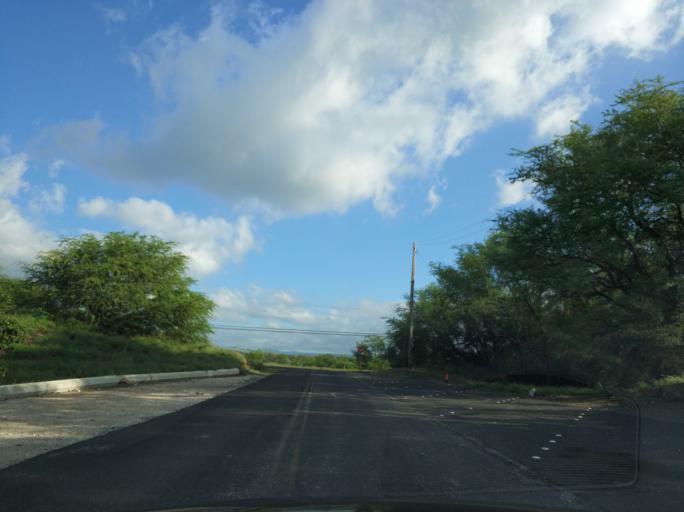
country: US
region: Hawaii
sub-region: Hawaii County
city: Waikoloa Village
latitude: 19.9738
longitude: -155.8310
